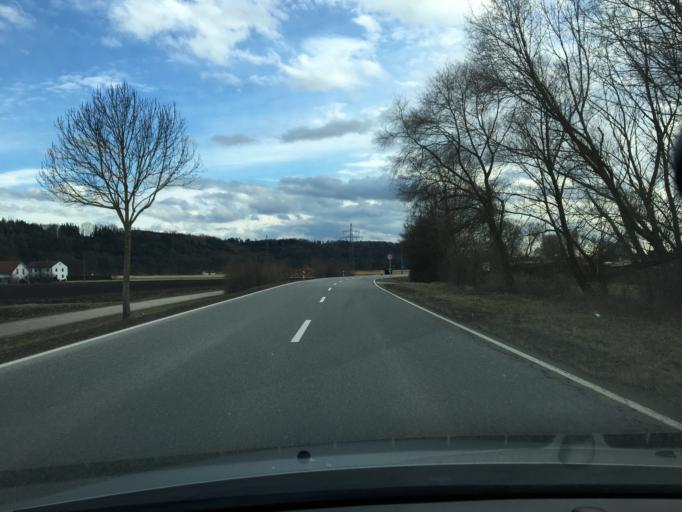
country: DE
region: Bavaria
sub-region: Lower Bavaria
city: Eching
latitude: 48.4820
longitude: 12.0166
